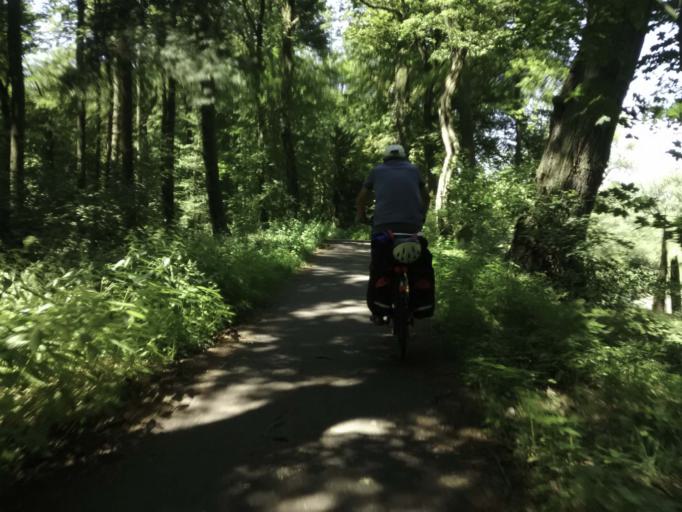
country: DE
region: Saxony-Anhalt
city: Vockerode
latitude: 51.8649
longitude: 12.3261
